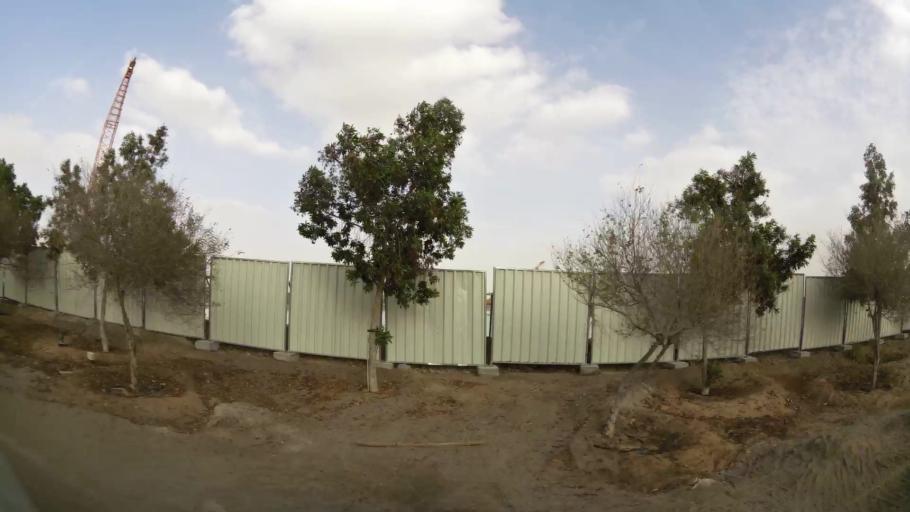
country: AE
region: Abu Dhabi
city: Abu Dhabi
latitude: 24.5043
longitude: 54.6026
